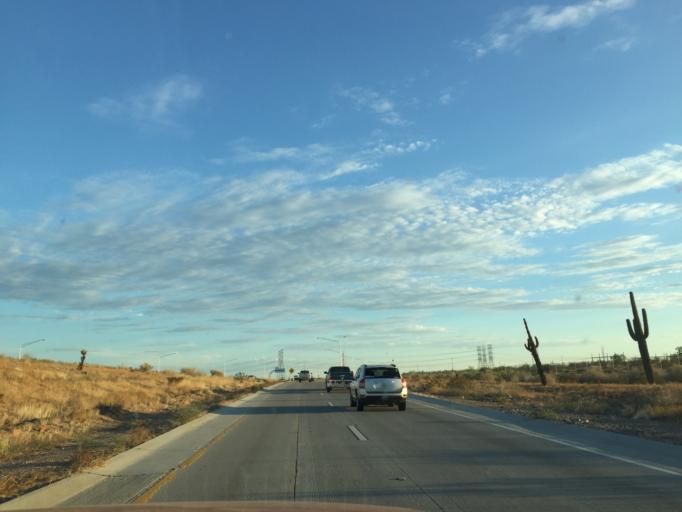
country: US
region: Arizona
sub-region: Maricopa County
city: Sun City West
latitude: 33.7123
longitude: -112.3119
